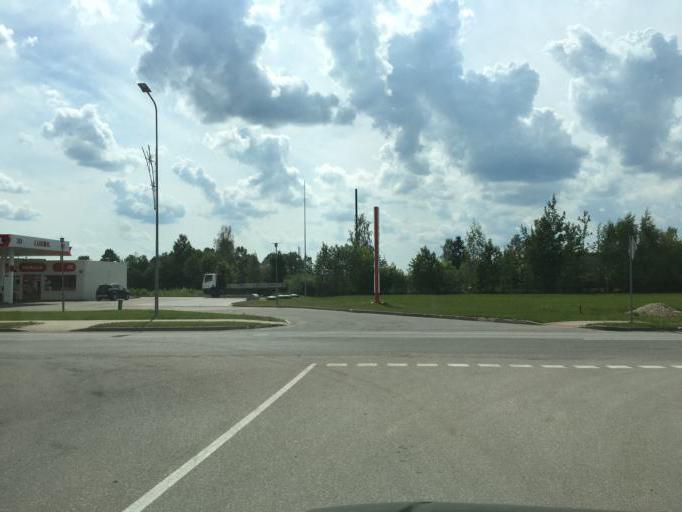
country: LV
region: Balvu Rajons
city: Balvi
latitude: 57.1421
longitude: 27.2452
